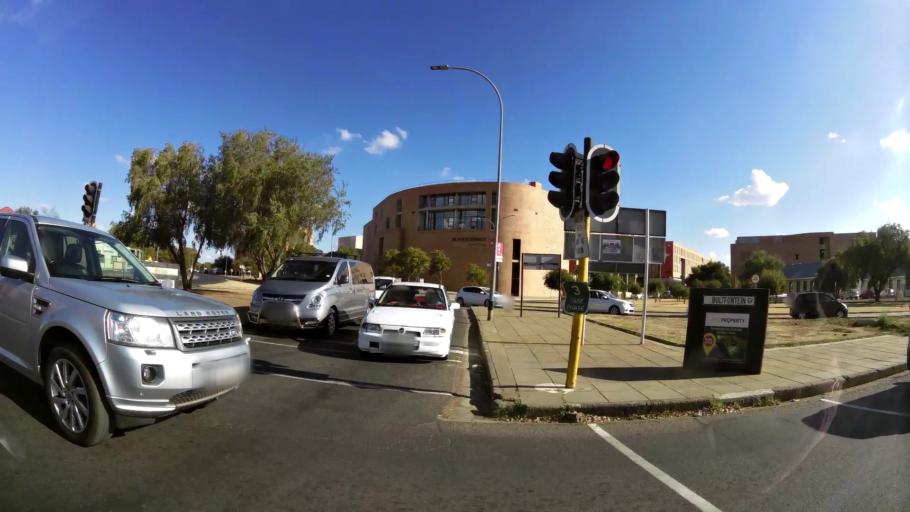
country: ZA
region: Northern Cape
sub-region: Frances Baard District Municipality
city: Kimberley
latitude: -28.7478
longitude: 24.7660
